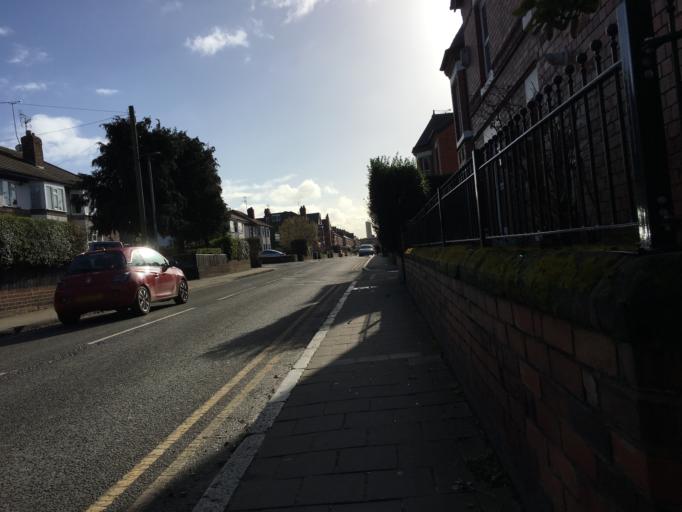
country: GB
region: England
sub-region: Cheshire West and Chester
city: Hoole
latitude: 53.2018
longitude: -2.8837
